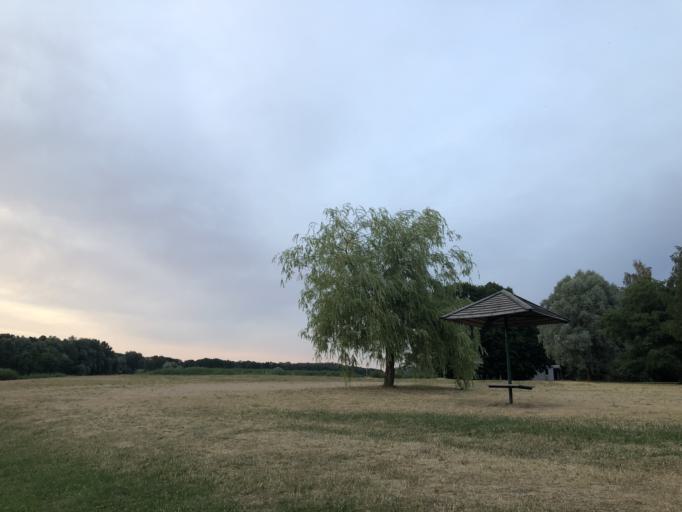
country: BY
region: Minsk
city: Nyasvizh
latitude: 53.2229
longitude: 26.6973
